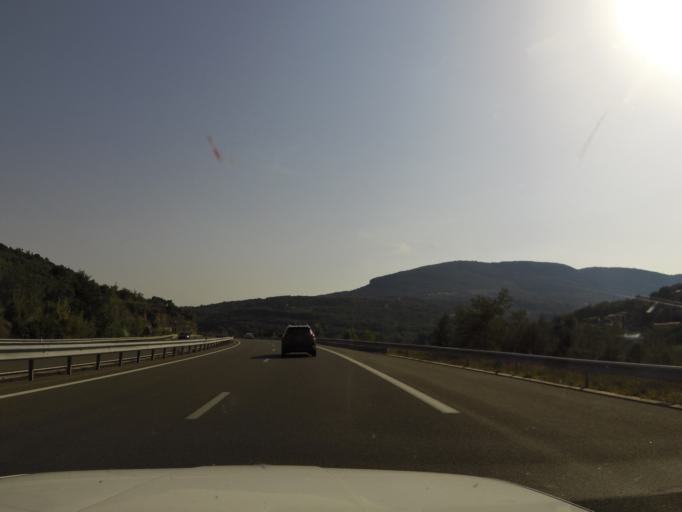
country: FR
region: Languedoc-Roussillon
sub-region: Departement de l'Herault
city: Lodeve
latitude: 43.7644
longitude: 3.3335
